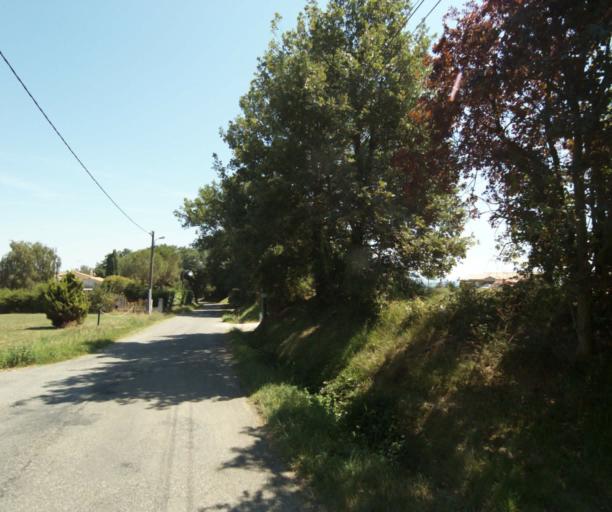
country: FR
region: Midi-Pyrenees
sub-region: Departement de l'Ariege
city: Lezat-sur-Leze
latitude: 43.2777
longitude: 1.3354
